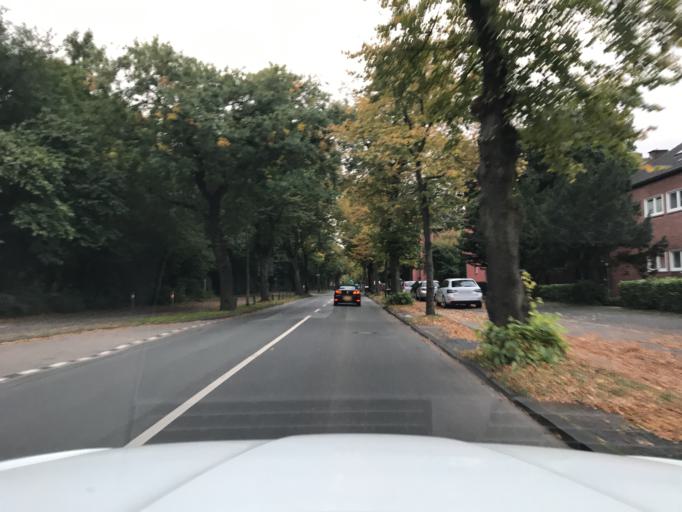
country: DE
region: North Rhine-Westphalia
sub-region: Regierungsbezirk Dusseldorf
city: Hochfeld
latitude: 51.3803
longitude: 6.7817
